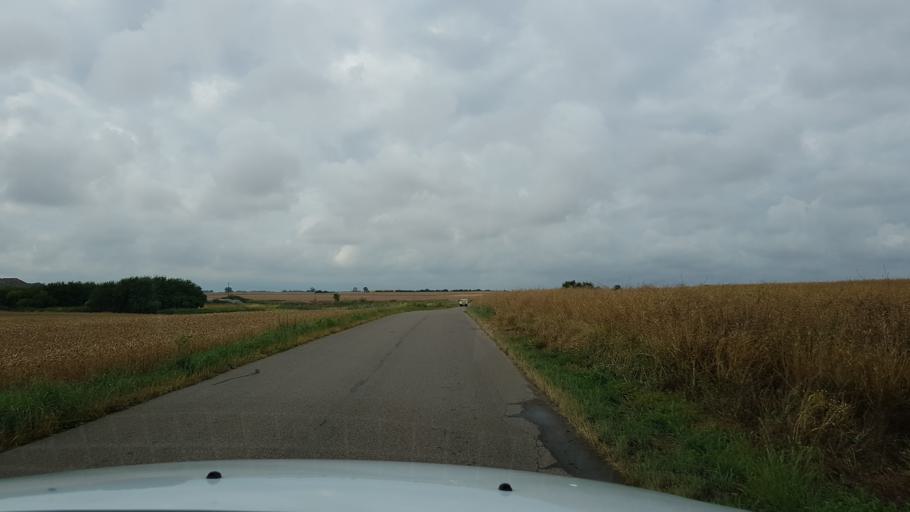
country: PL
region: West Pomeranian Voivodeship
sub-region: Powiat pyrzycki
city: Przelewice
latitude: 53.0836
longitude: 15.1473
